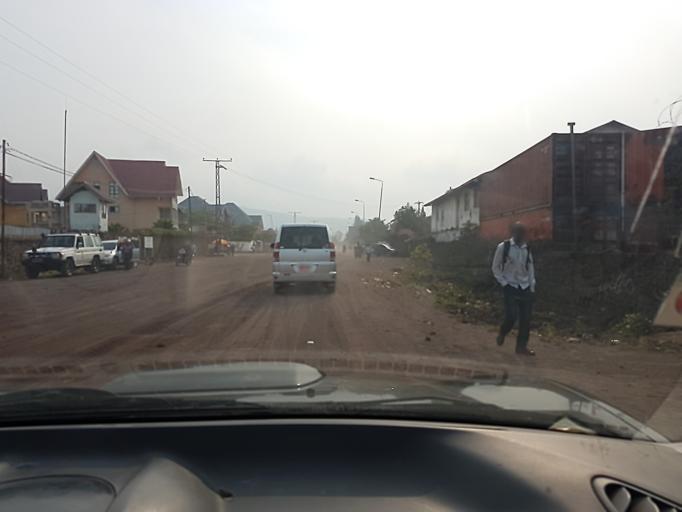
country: CD
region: Nord Kivu
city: Goma
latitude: -1.6880
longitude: 29.2336
